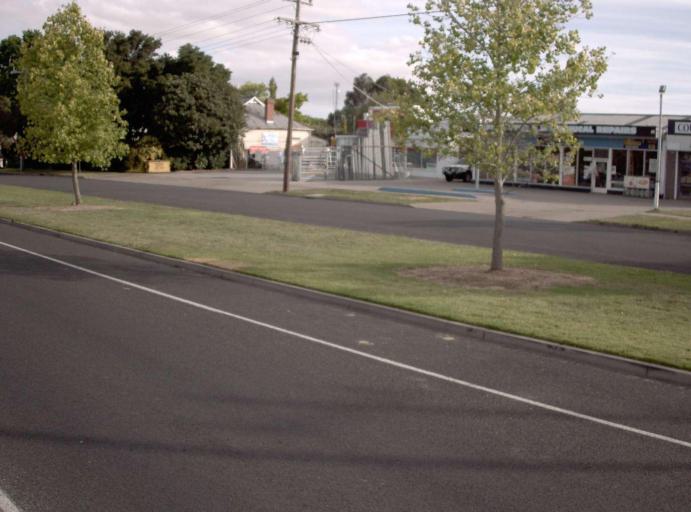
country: AU
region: Victoria
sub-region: Wellington
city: Sale
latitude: -37.9684
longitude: 146.9789
